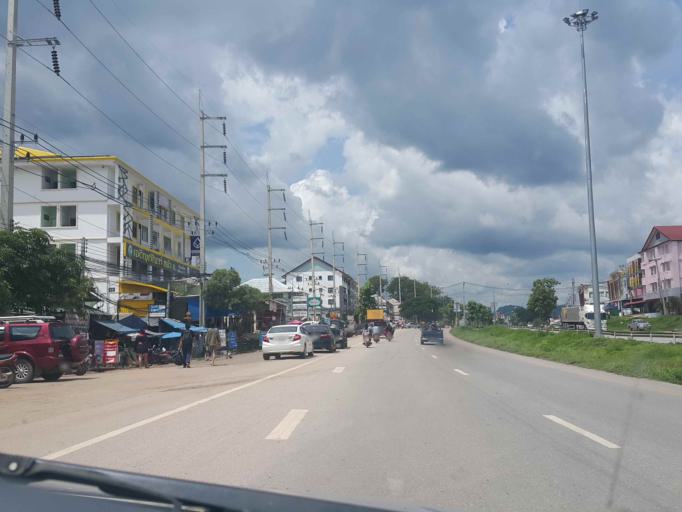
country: TH
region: Phayao
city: Dok Kham Tai
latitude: 19.0298
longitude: 99.9261
